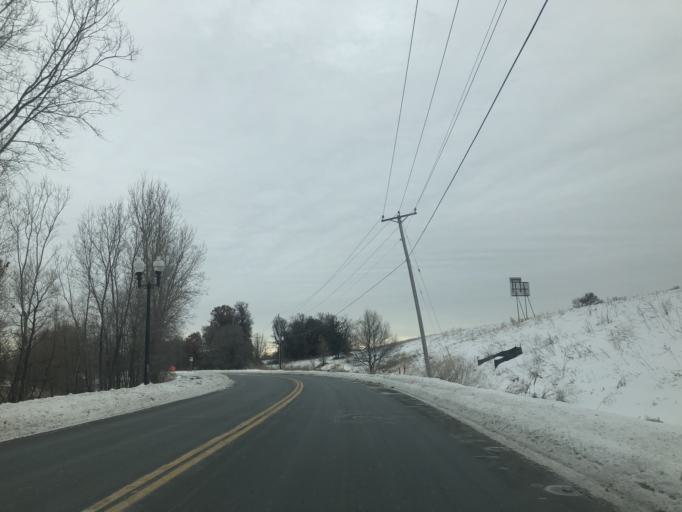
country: US
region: Minnesota
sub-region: Ramsey County
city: Mounds View
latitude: 45.1109
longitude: -93.1877
